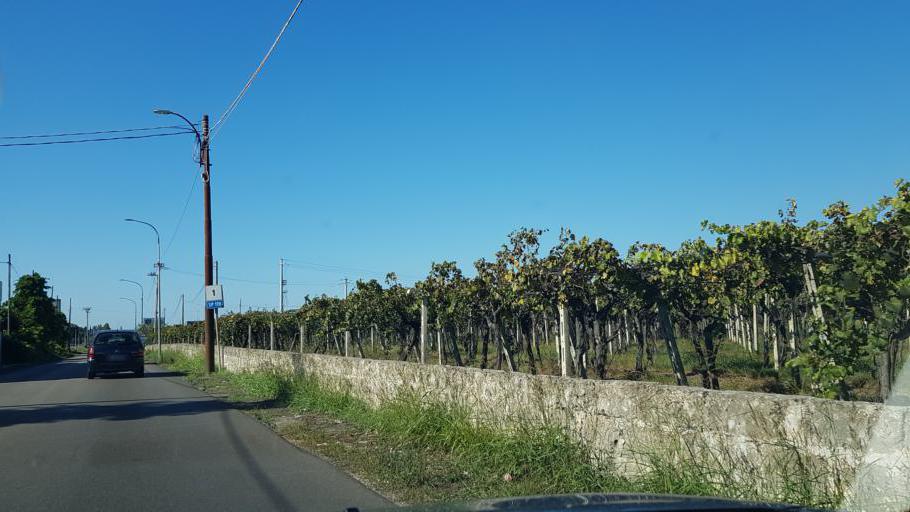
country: IT
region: Apulia
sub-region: Provincia di Lecce
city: Arnesano
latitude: 40.3321
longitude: 18.0920
